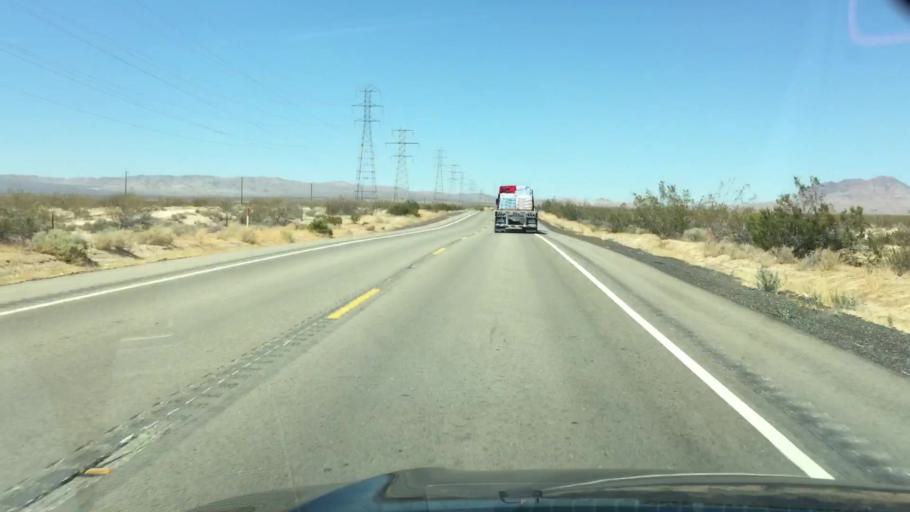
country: US
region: California
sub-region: Kern County
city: Boron
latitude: 35.2224
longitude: -117.6057
